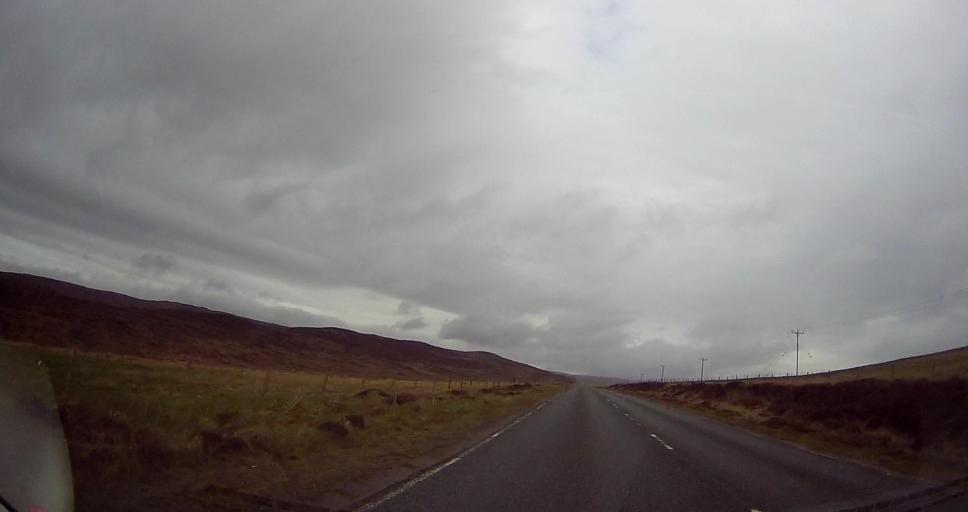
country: GB
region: Scotland
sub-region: Shetland Islands
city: Lerwick
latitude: 60.2027
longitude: -1.2333
